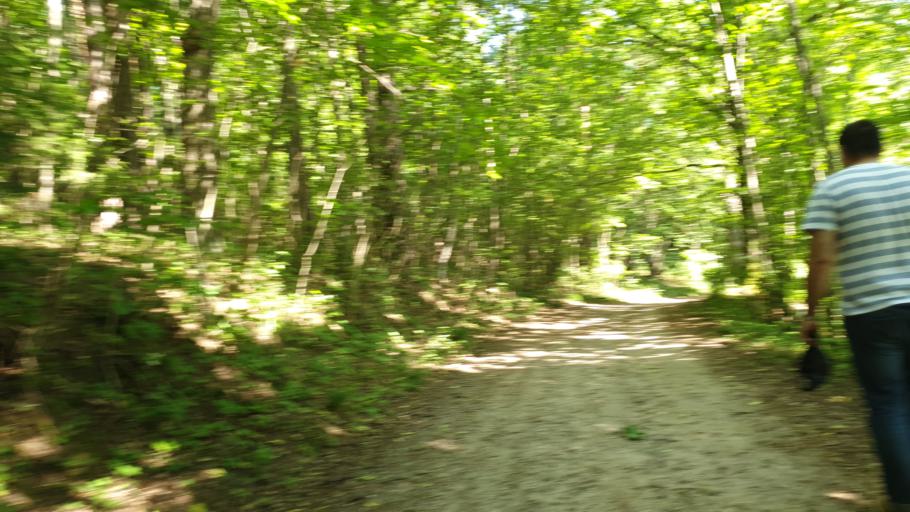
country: LT
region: Vilnius County
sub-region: Vilnius
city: Fabijoniskes
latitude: 54.7902
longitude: 25.3113
